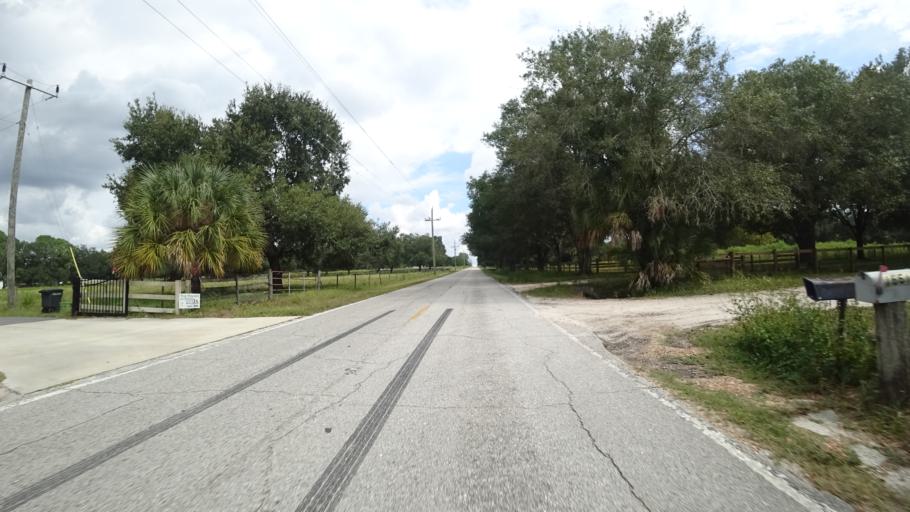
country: US
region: Florida
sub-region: Manatee County
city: Ellenton
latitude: 27.4878
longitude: -82.3747
